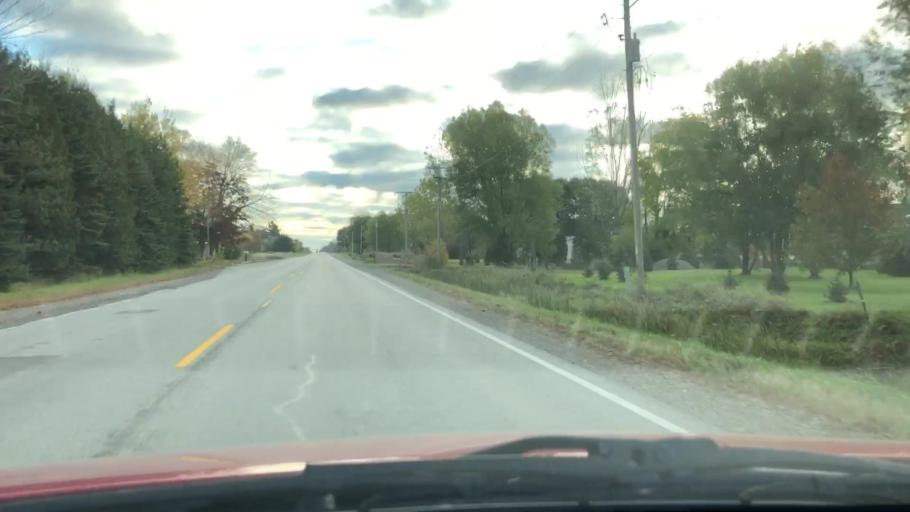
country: US
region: Wisconsin
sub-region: Brown County
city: Oneida
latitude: 44.4442
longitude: -88.2098
